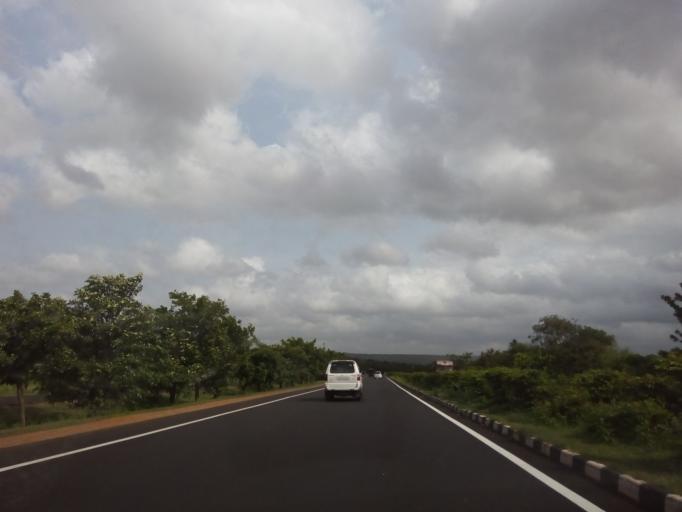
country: IN
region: Karnataka
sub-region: Belgaum
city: Hukeri
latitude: 16.1001
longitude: 74.5184
